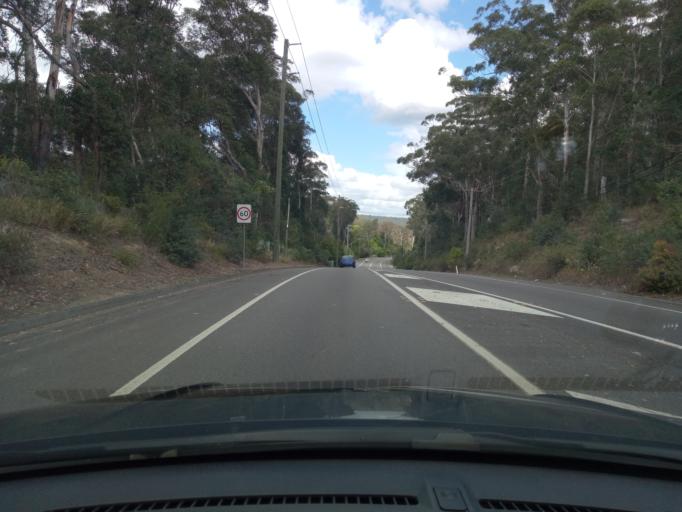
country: AU
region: New South Wales
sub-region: Gosford Shire
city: Narara
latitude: -33.4086
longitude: 151.3364
